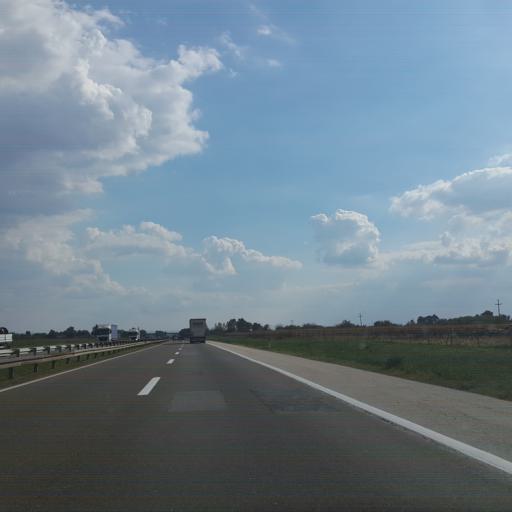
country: RS
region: Central Serbia
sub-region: Podunavski Okrug
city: Velika Plana
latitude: 44.3155
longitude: 21.0924
